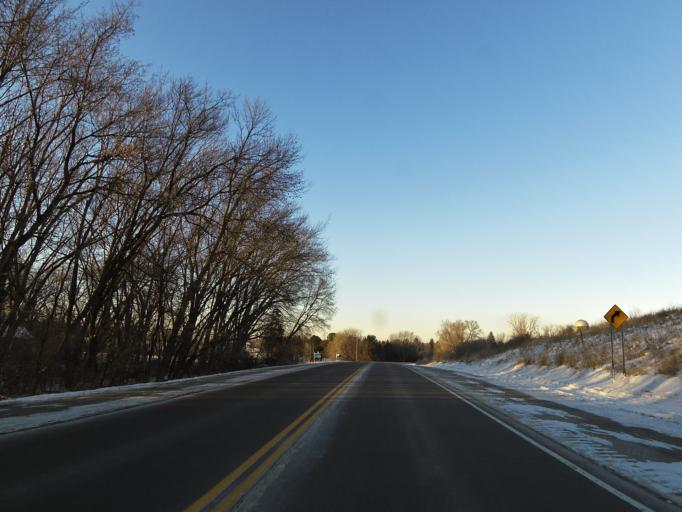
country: US
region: Minnesota
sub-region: Dakota County
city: Farmington
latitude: 44.5598
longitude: -93.1360
